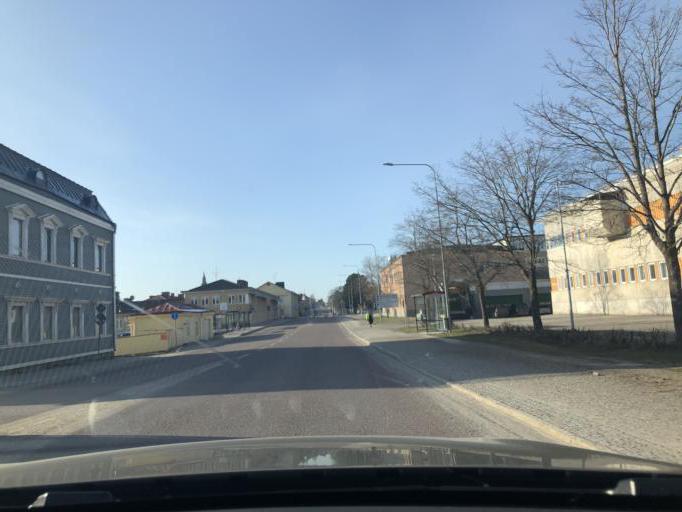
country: SE
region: Gaevleborg
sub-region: Hudiksvalls Kommun
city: Hudiksvall
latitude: 61.7310
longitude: 17.1004
